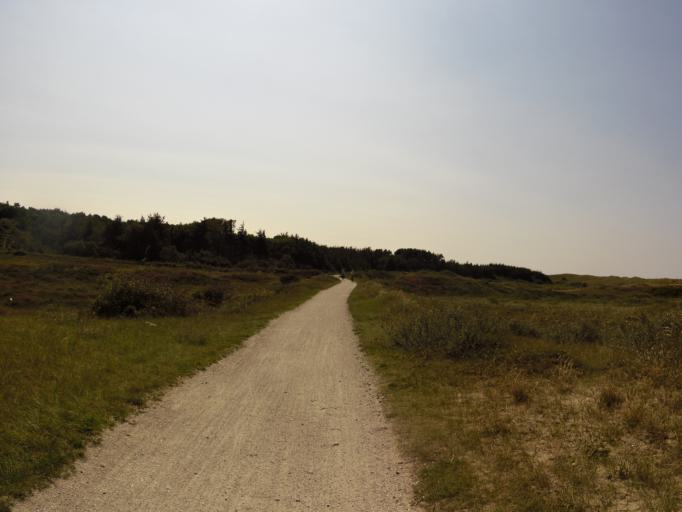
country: NL
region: North Holland
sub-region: Gemeente Schagen
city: Harenkarspel
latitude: 52.7804
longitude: 4.6706
